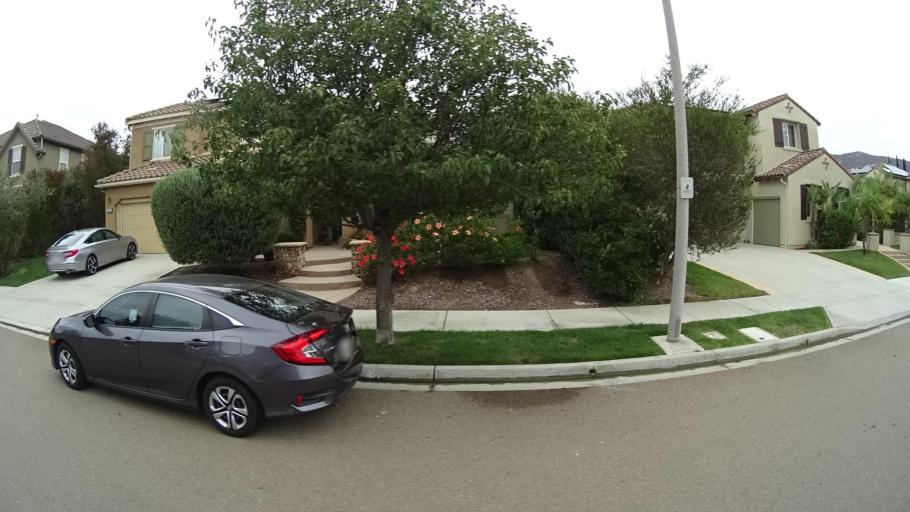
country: US
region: California
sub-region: San Diego County
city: Fairbanks Ranch
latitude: 33.0276
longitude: -117.1167
